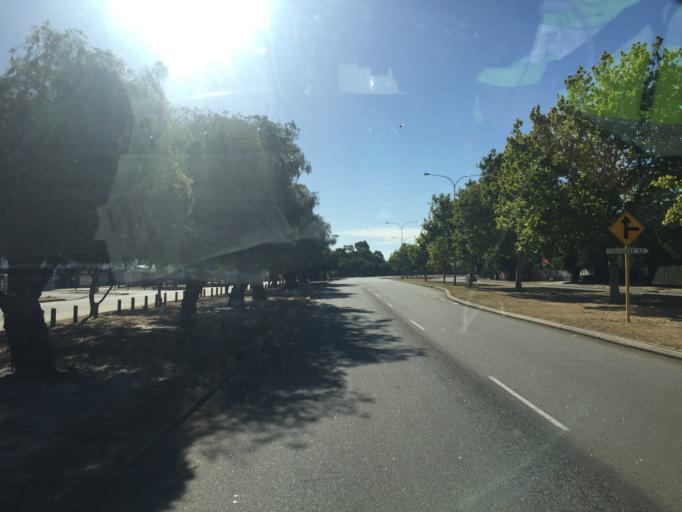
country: AU
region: Western Australia
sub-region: Canning
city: Queens Park
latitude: -31.9953
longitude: 115.9491
